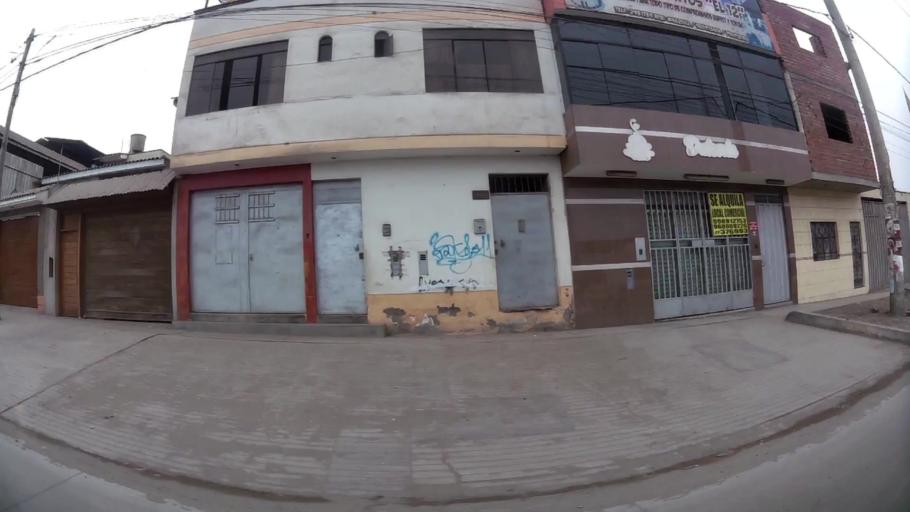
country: PE
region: Lima
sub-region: Lima
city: Surco
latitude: -12.2262
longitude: -76.9087
